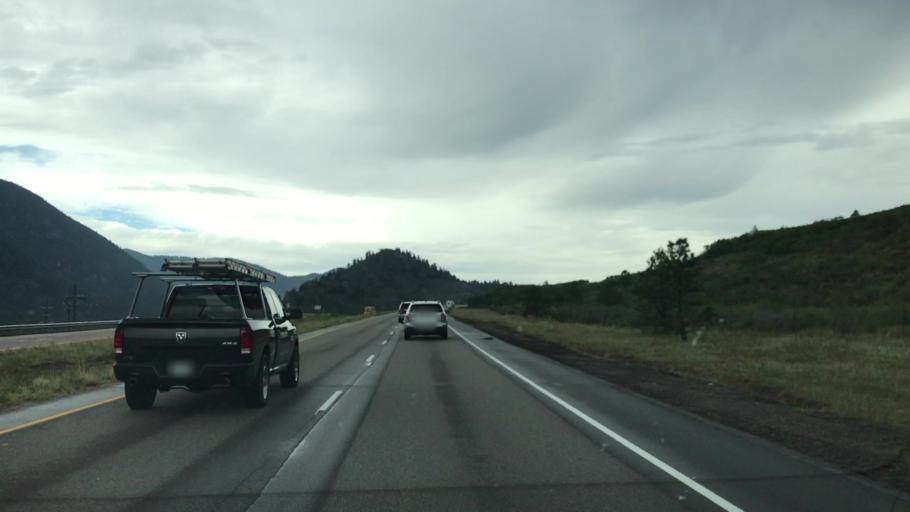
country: US
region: Colorado
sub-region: El Paso County
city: Cascade-Chipita Park
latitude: 38.9234
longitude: -104.9931
